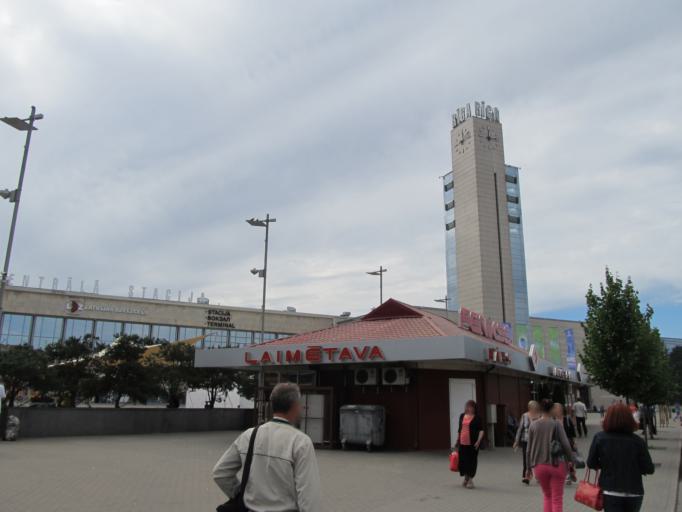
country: LV
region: Riga
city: Riga
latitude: 56.9477
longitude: 24.1204
